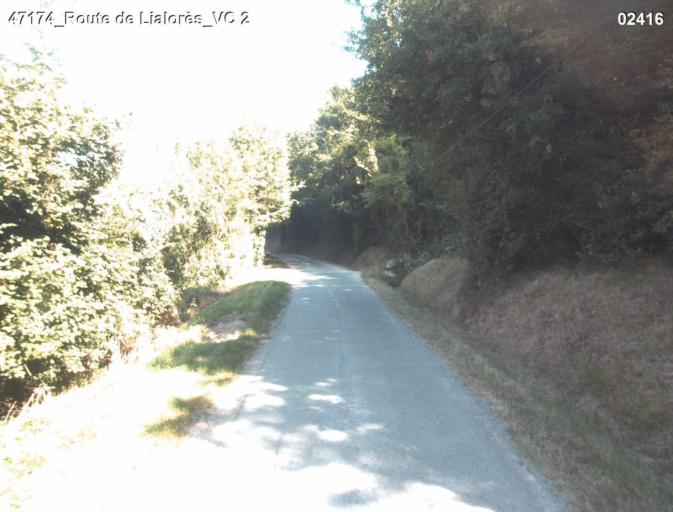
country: FR
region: Midi-Pyrenees
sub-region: Departement du Gers
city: Condom
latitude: 44.0249
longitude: 0.3699
